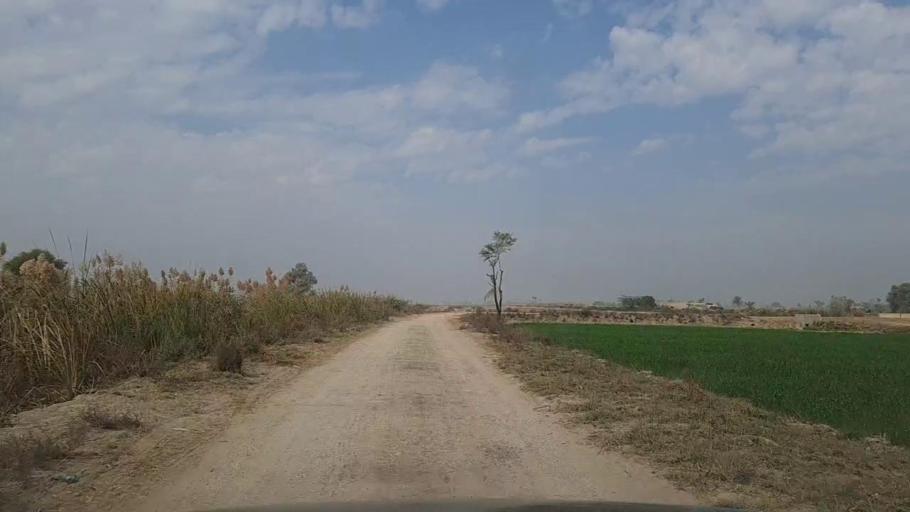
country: PK
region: Sindh
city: Daur
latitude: 26.3978
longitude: 68.3472
